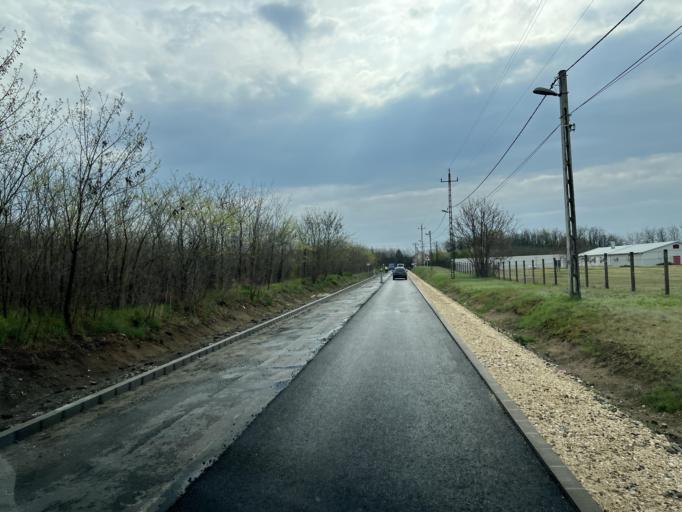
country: HU
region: Pest
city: Danszentmiklos
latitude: 47.2185
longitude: 19.5282
